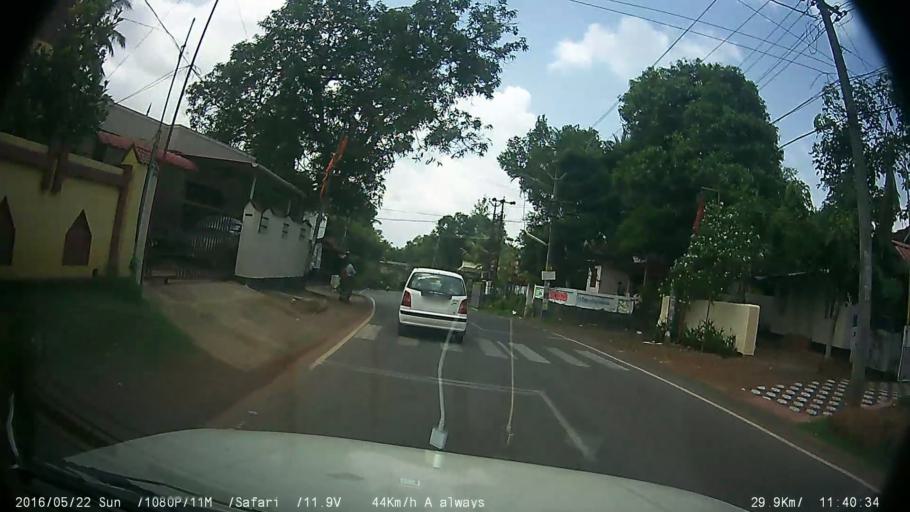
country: IN
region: Kerala
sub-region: Kottayam
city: Kottayam
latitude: 9.5543
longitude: 76.5176
